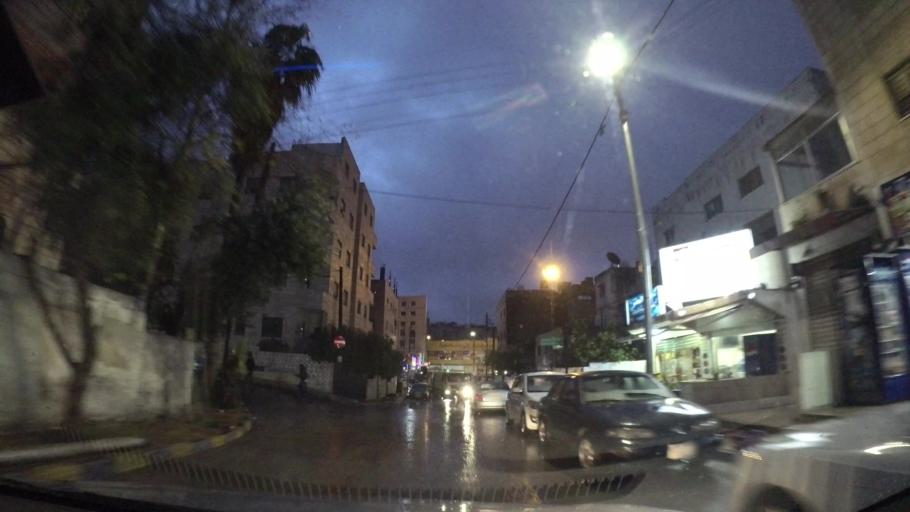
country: JO
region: Amman
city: Al Jubayhah
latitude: 32.0231
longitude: 35.8453
